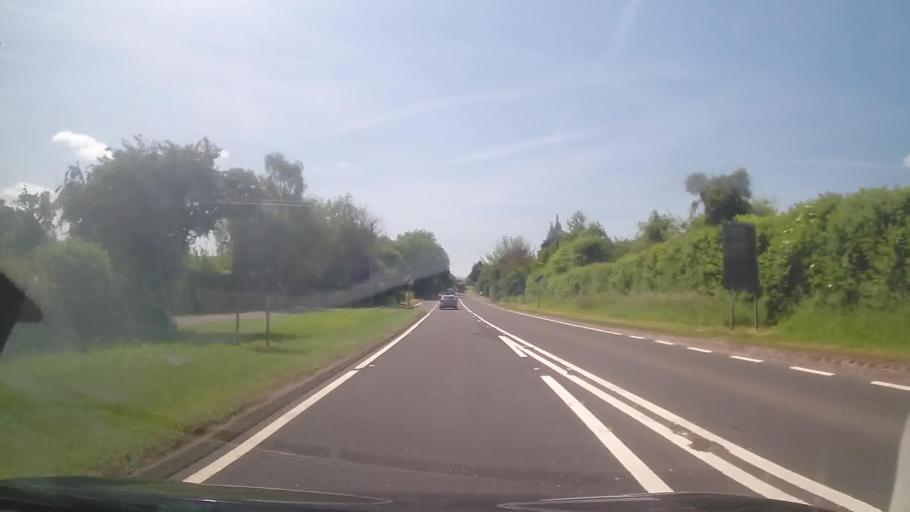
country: GB
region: England
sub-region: Herefordshire
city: Dinmore
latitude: 52.1481
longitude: -2.7276
